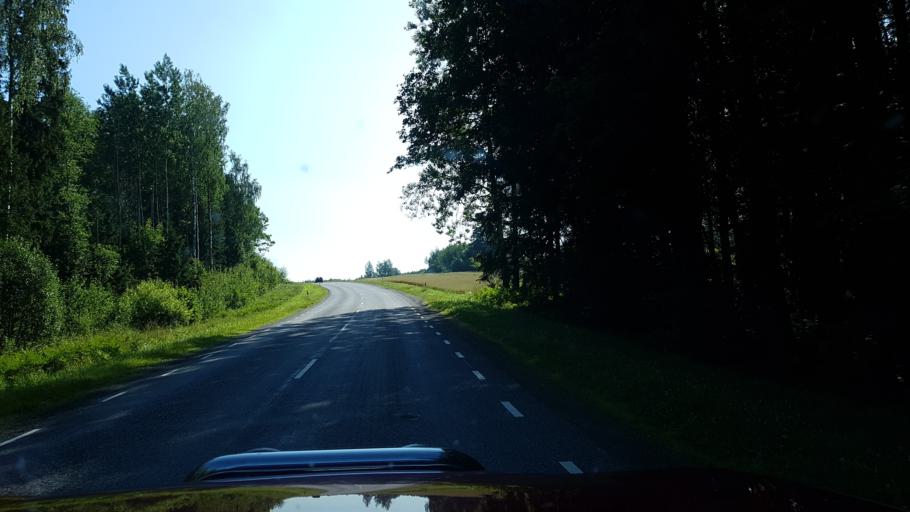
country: EE
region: Vorumaa
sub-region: Voru linn
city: Voru
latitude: 57.9760
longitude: 26.8026
